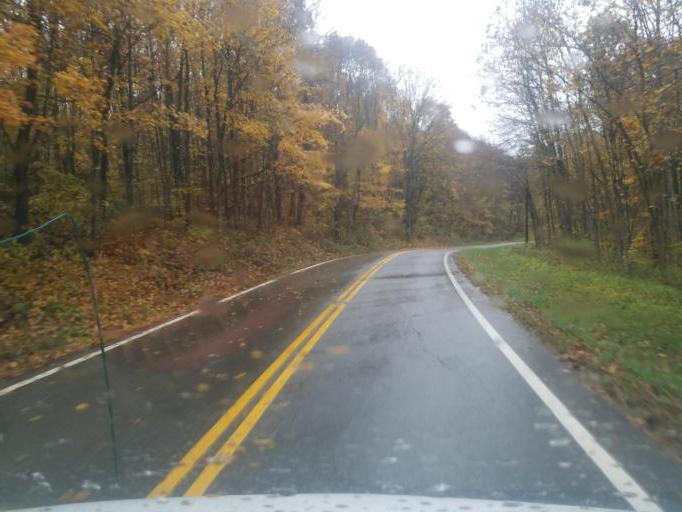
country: US
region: Ohio
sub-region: Washington County
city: Beverly
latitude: 39.4741
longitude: -81.7274
